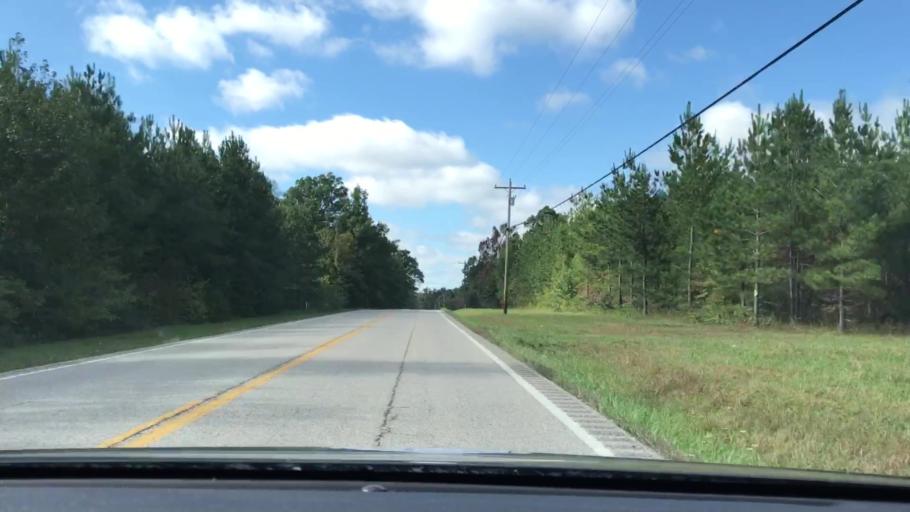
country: US
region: Tennessee
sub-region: Scott County
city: Huntsville
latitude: 36.3429
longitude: -84.6508
